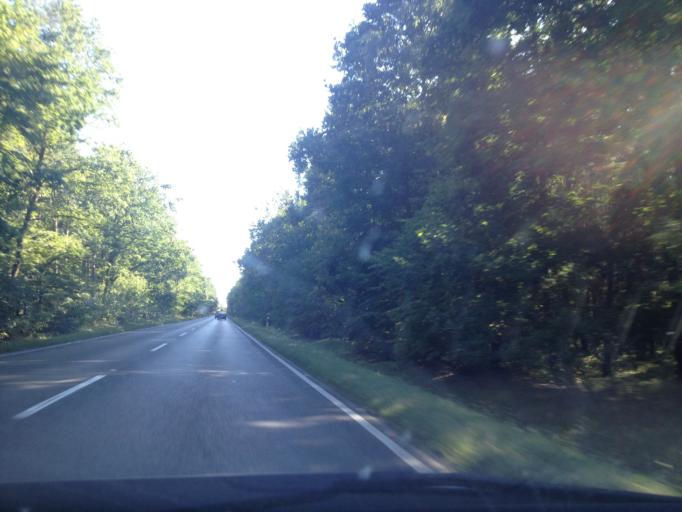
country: PL
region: Greater Poland Voivodeship
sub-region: Powiat poznanski
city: Kornik
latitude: 52.1957
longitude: 17.0616
